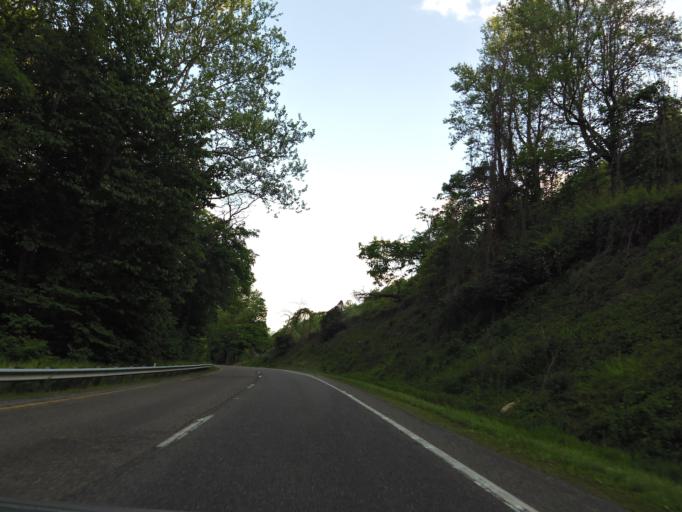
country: US
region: Virginia
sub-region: Russell County
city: Lebanon
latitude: 36.8026
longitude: -82.0949
